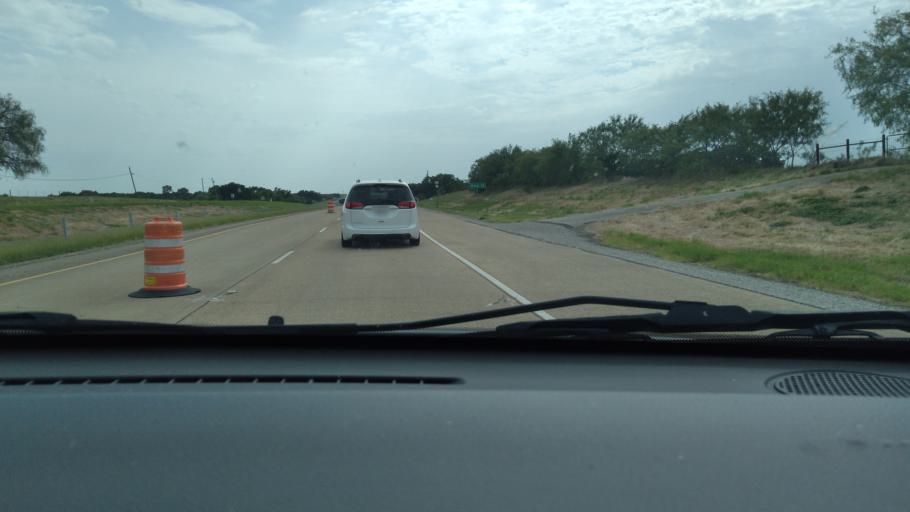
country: US
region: Texas
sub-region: Hill County
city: Hubbard
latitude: 31.8821
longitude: -96.7501
